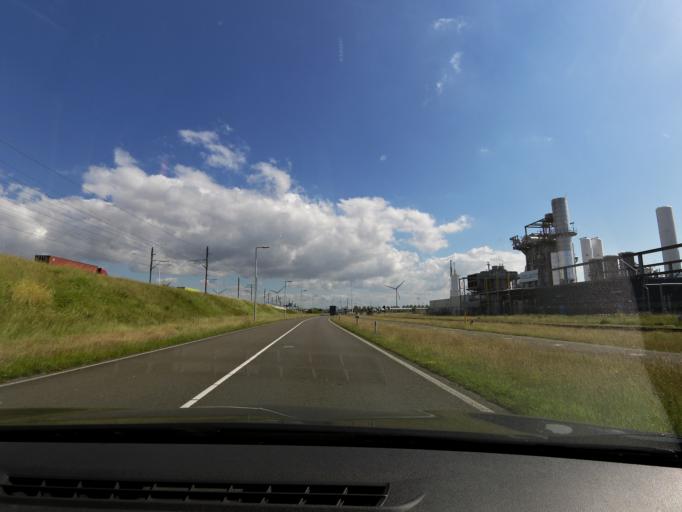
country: NL
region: South Holland
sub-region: Gemeente Maassluis
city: Maassluis
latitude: 51.8802
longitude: 4.2604
